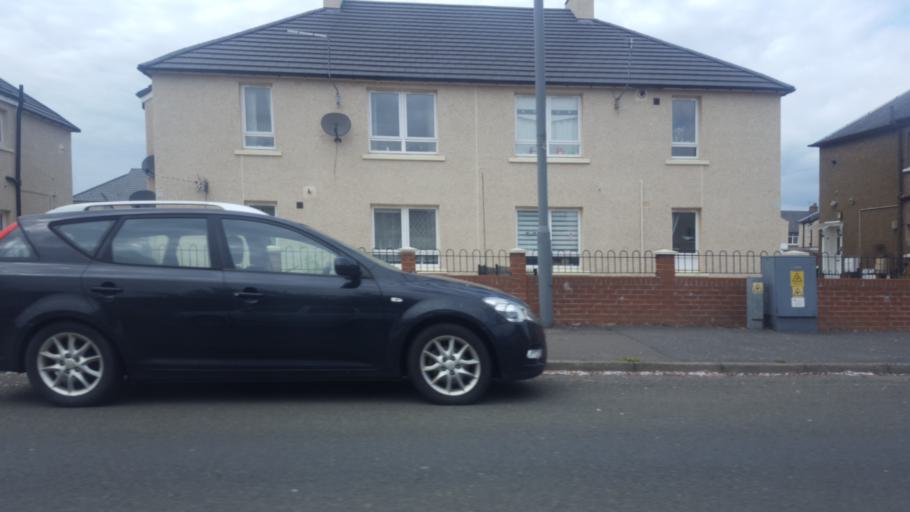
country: GB
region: Scotland
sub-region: Falkirk
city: Grangemouth
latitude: 56.0085
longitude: -3.7256
